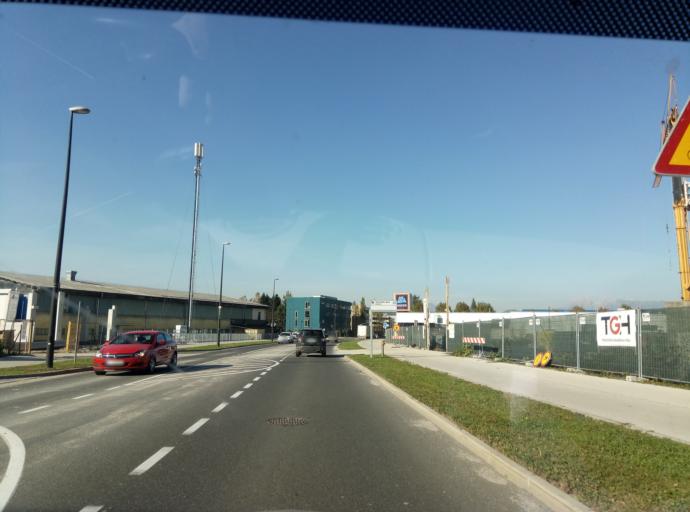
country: SI
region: Ljubljana
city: Ljubljana
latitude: 46.0456
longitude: 14.4620
